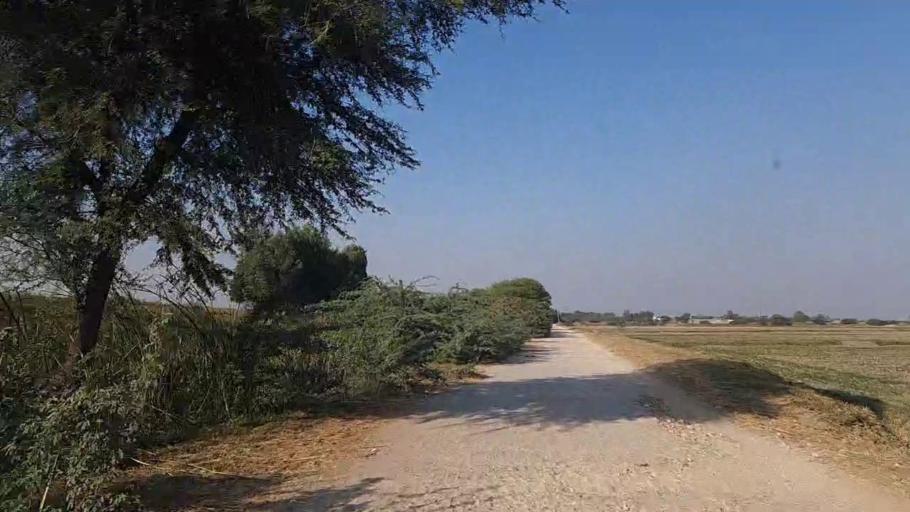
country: PK
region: Sindh
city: Thatta
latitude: 24.7528
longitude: 67.9608
